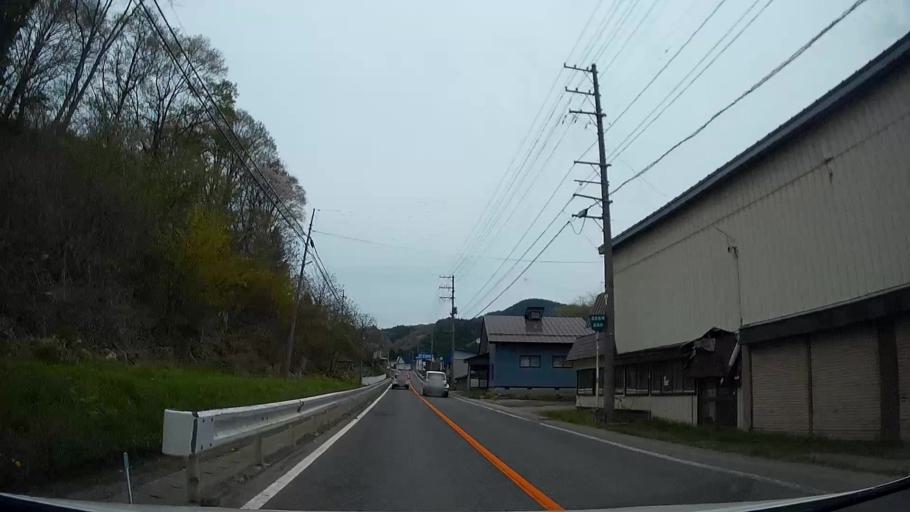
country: JP
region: Akita
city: Hanawa
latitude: 40.2995
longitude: 140.8388
